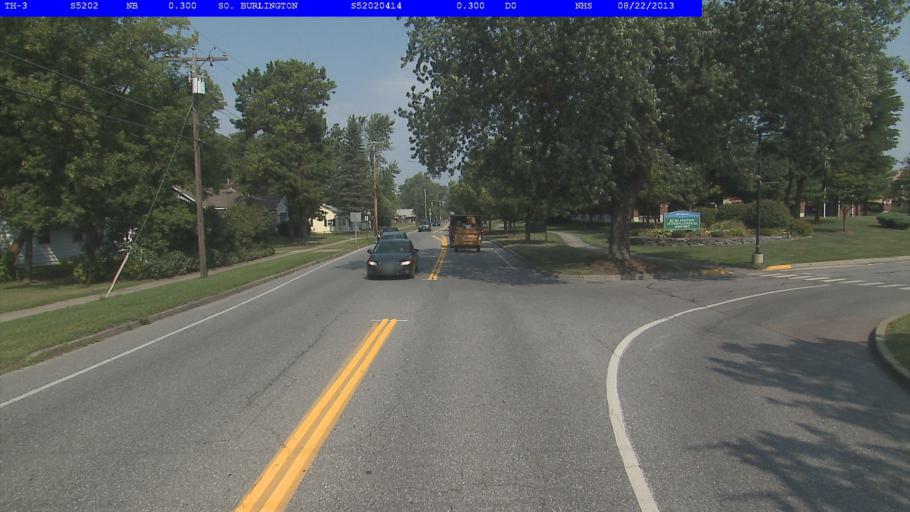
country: US
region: Vermont
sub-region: Chittenden County
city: South Burlington
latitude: 44.4672
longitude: -73.1559
